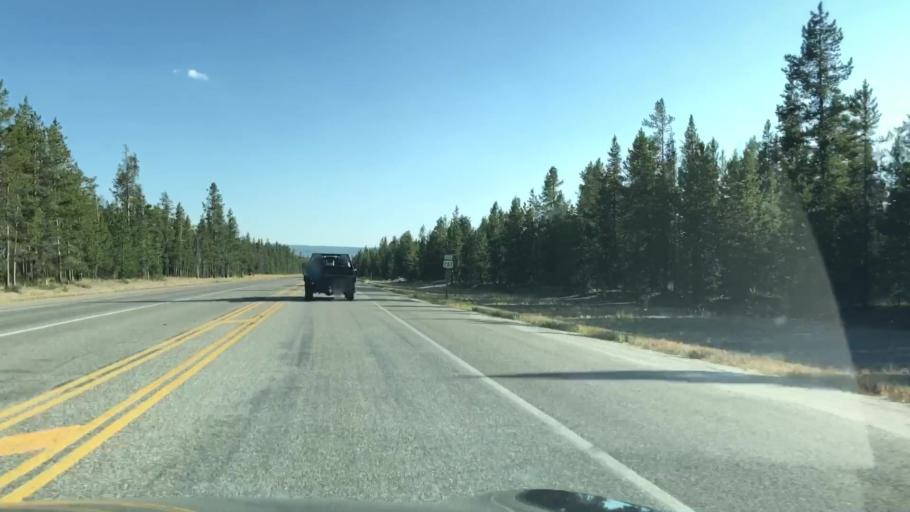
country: US
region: Montana
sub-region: Gallatin County
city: West Yellowstone
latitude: 44.6868
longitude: -111.1012
